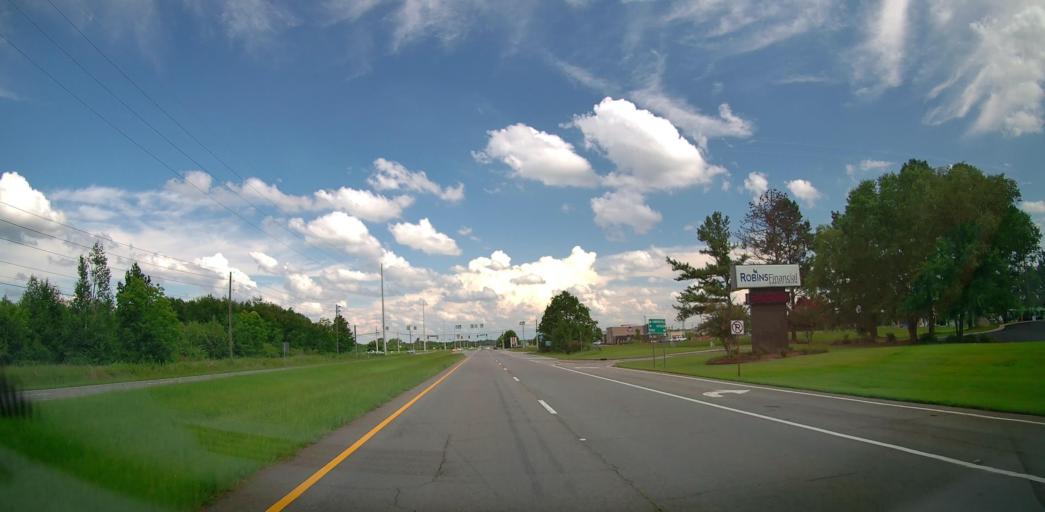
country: US
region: Georgia
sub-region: Houston County
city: Perry
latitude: 32.4768
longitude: -83.7071
